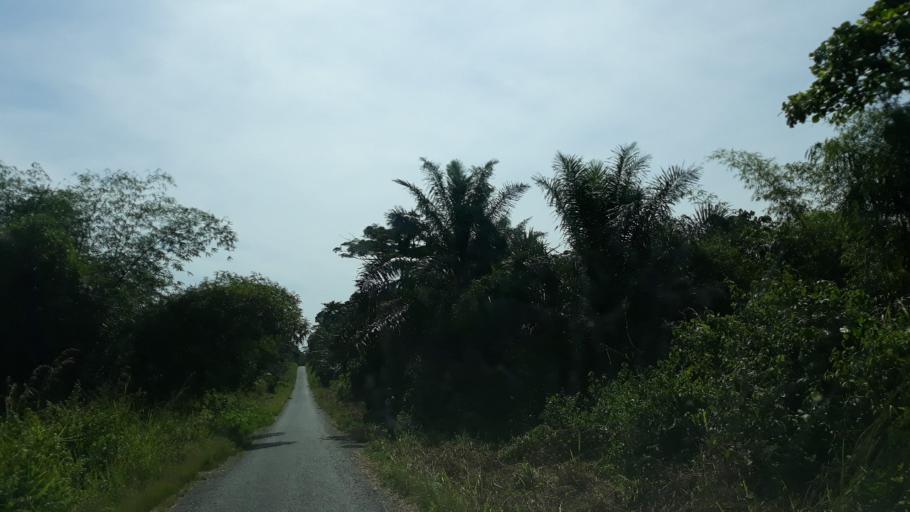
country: CD
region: Maniema
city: Kindu
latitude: -2.9059
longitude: 26.0323
